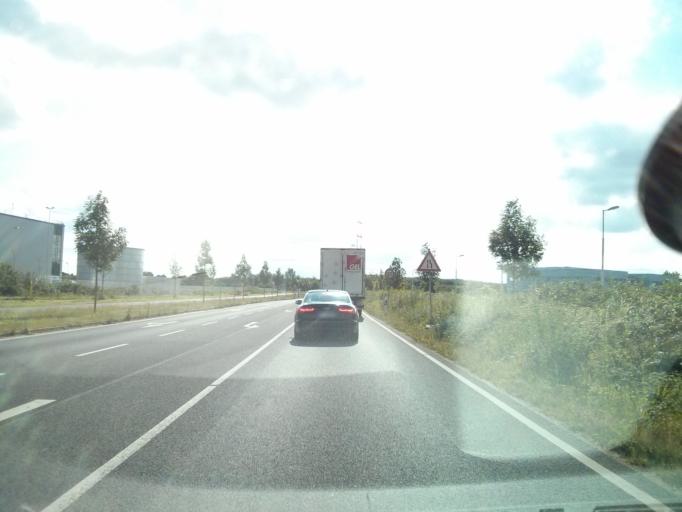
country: DE
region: North Rhine-Westphalia
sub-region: Regierungsbezirk Dusseldorf
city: Willich
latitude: 51.2947
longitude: 6.5457
